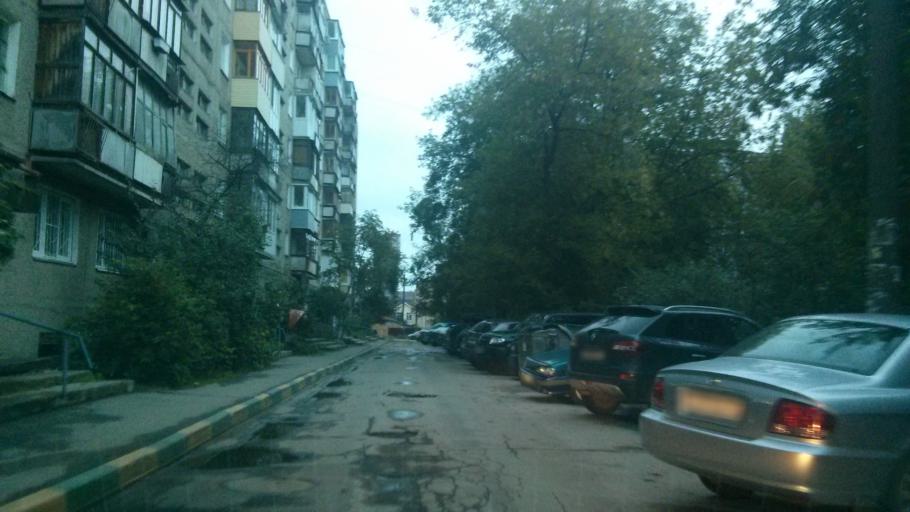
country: RU
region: Nizjnij Novgorod
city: Nizhniy Novgorod
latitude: 56.3023
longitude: 44.0369
